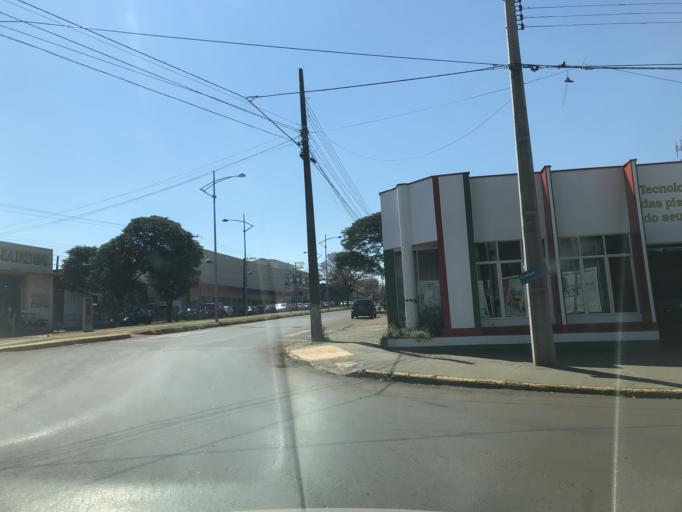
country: BR
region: Parana
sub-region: Toledo
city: Toledo
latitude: -24.7254
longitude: -53.7244
